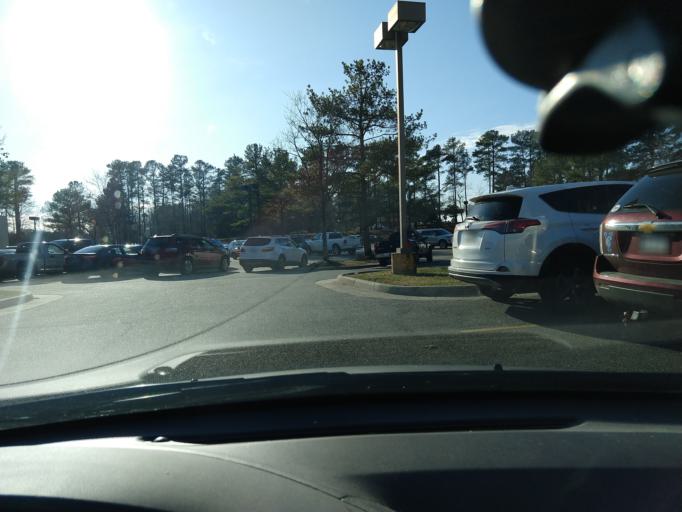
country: US
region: Virginia
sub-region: James City County
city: Williamsburg
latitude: 37.2520
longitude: -76.7640
